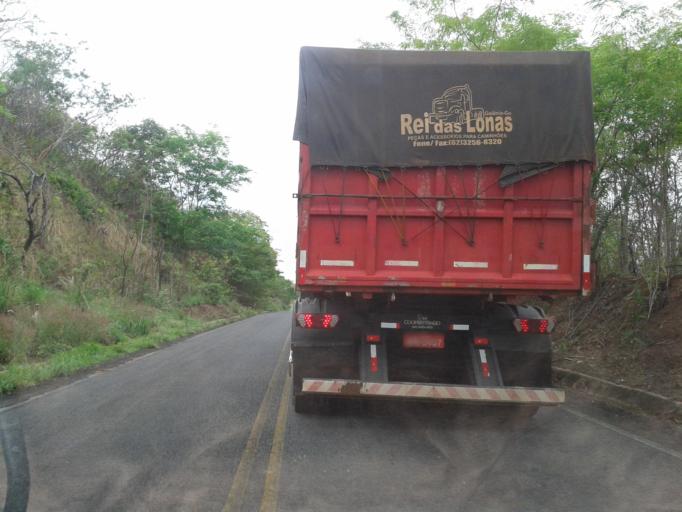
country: BR
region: Goias
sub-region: Caldas Novas
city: Caldas Novas
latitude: -18.0623
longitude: -48.6920
